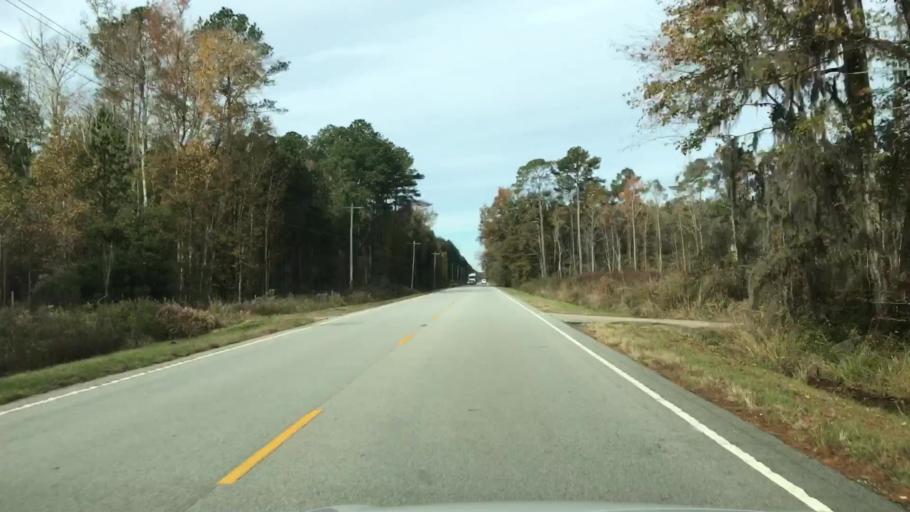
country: US
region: South Carolina
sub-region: Colleton County
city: Walterboro
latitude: 32.8120
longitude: -80.5299
